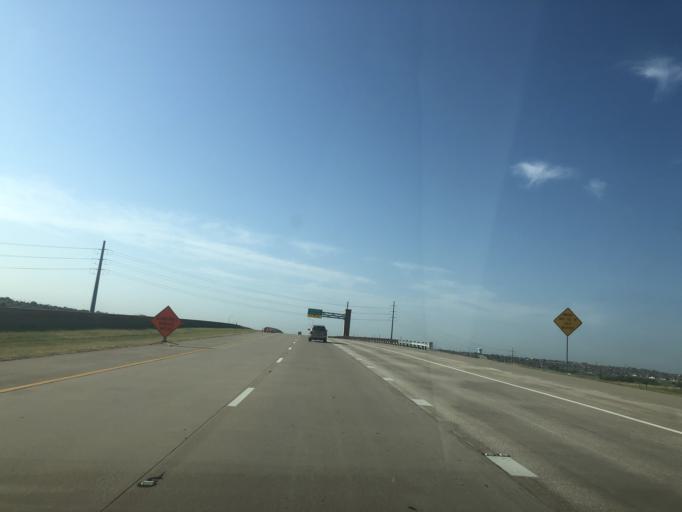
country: US
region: Texas
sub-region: Tarrant County
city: Benbrook
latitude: 32.6374
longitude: -97.4161
